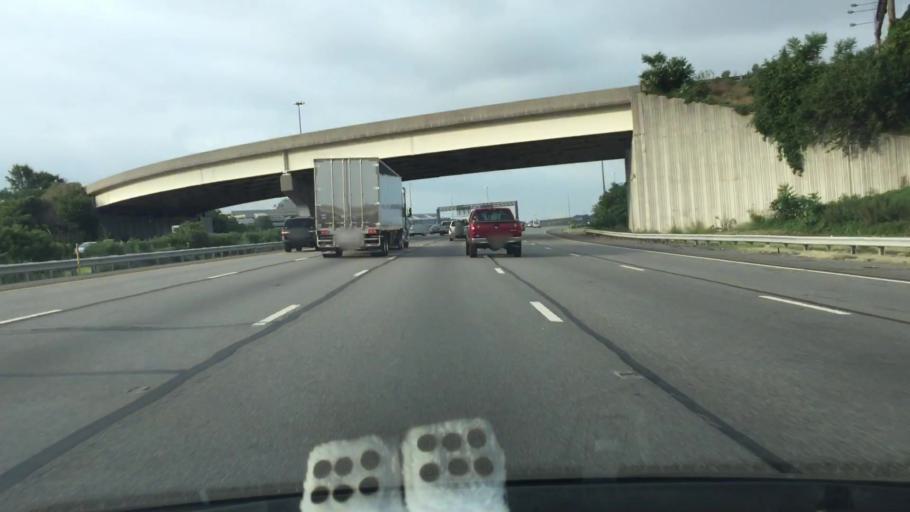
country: US
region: Pennsylvania
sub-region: Delaware County
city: Colwyn
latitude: 39.8823
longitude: -75.2425
